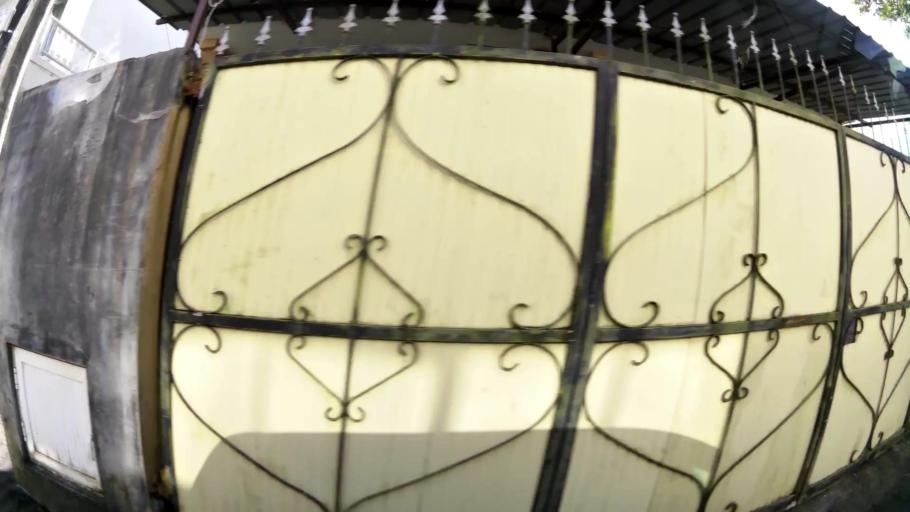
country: MU
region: Plaines Wilhems
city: Curepipe
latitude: -20.2904
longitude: 57.5157
